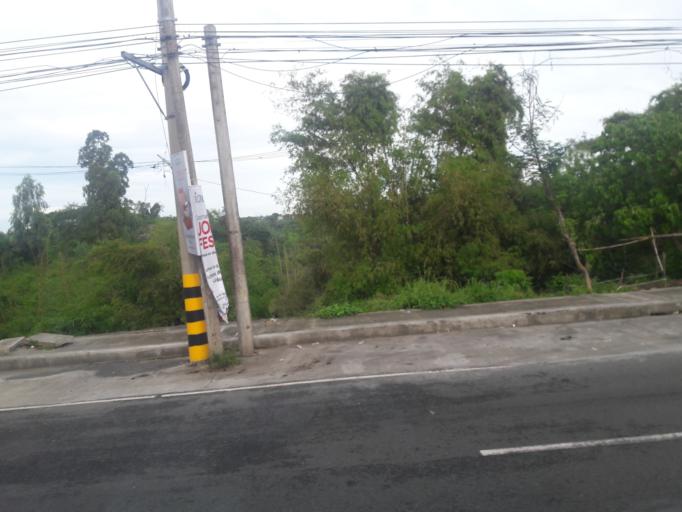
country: PH
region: Calabarzon
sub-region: Province of Cavite
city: Carmona
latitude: 14.3072
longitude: 121.0282
